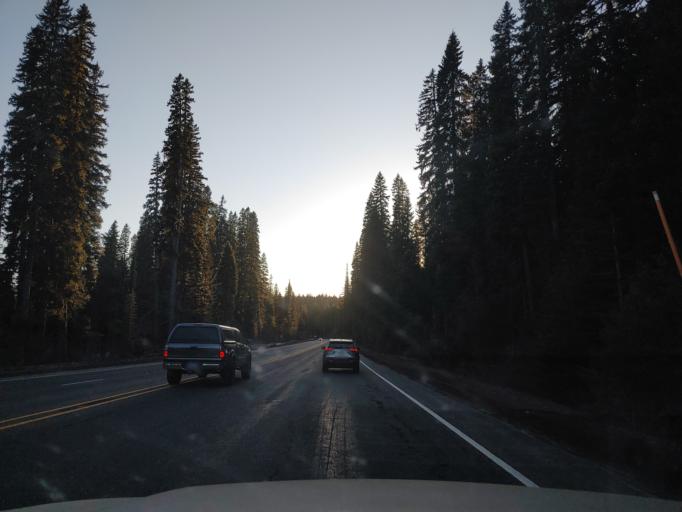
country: US
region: Oregon
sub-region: Lane County
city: Oakridge
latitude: 43.6167
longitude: -122.0933
